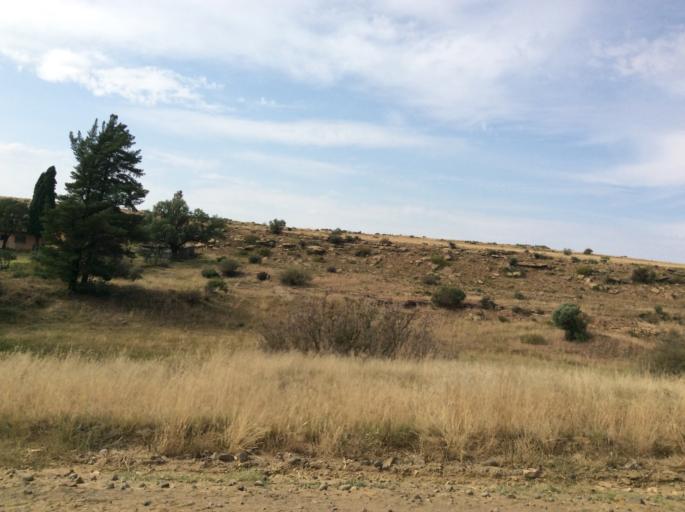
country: ZA
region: Orange Free State
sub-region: Xhariep District Municipality
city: Dewetsdorp
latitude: -29.5926
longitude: 26.6655
